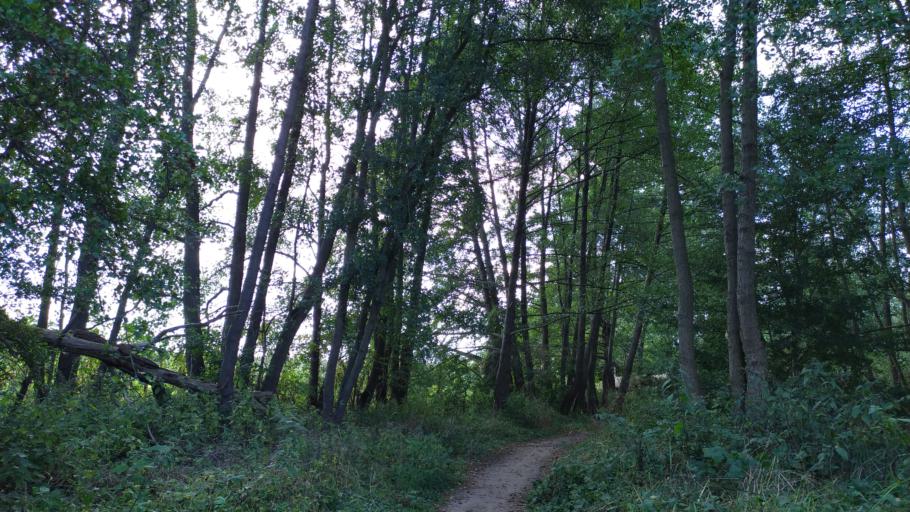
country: DE
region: Mecklenburg-Vorpommern
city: Lassan
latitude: 54.0074
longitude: 13.8657
